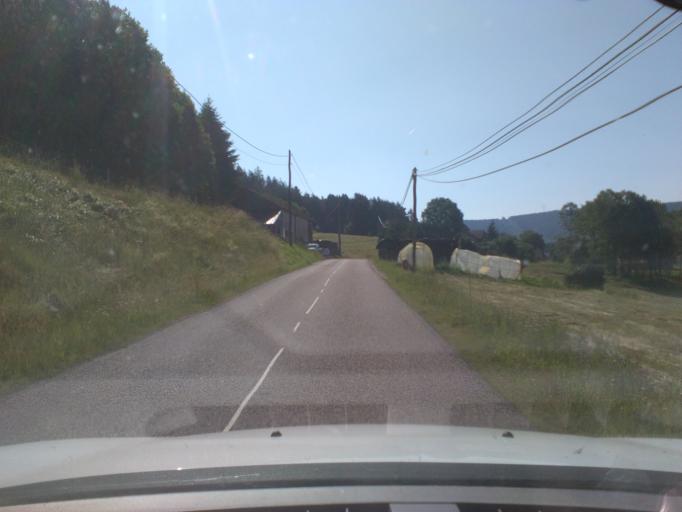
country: FR
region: Lorraine
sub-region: Departement des Vosges
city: Bruyeres
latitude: 48.2394
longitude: 6.7458
